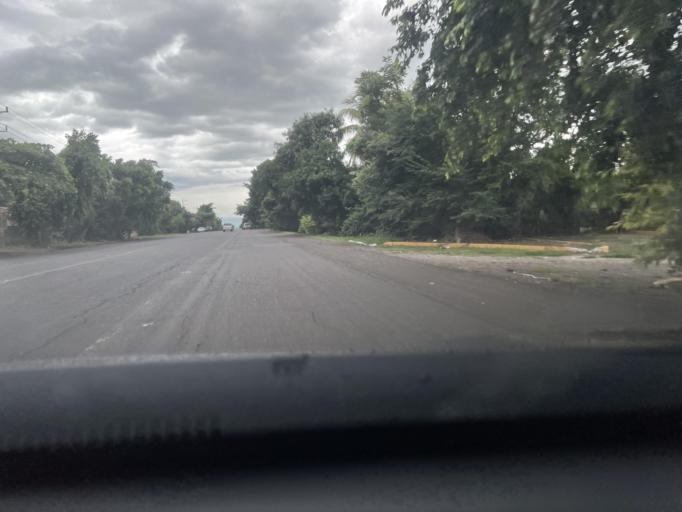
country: SV
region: Ahuachapan
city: Atiquizaya
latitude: 13.9717
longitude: -89.7382
